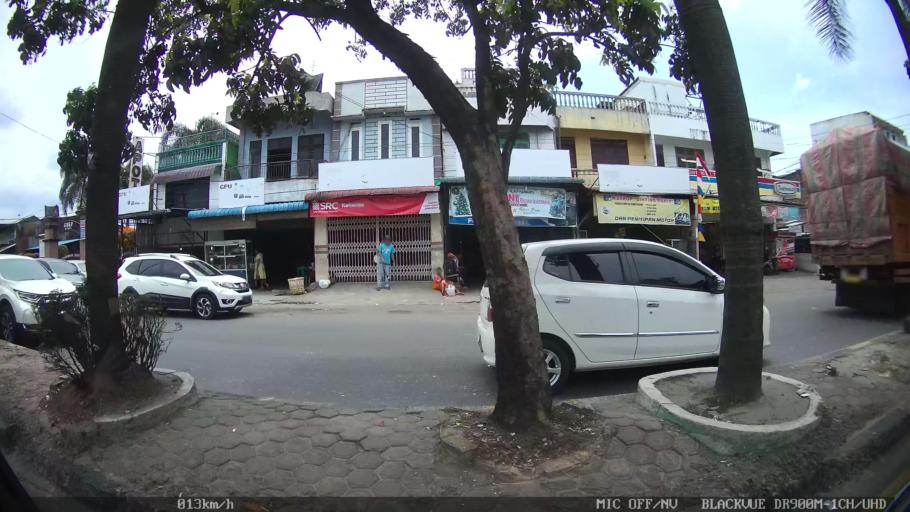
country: ID
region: North Sumatra
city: Deli Tua
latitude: 3.5397
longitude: 98.6535
